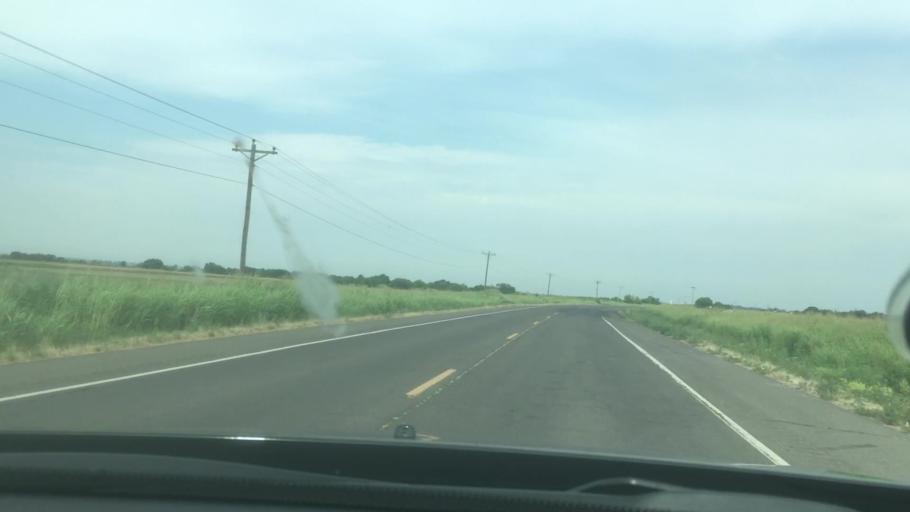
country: US
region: Oklahoma
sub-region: Garvin County
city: Maysville
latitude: 34.8191
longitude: -97.4846
